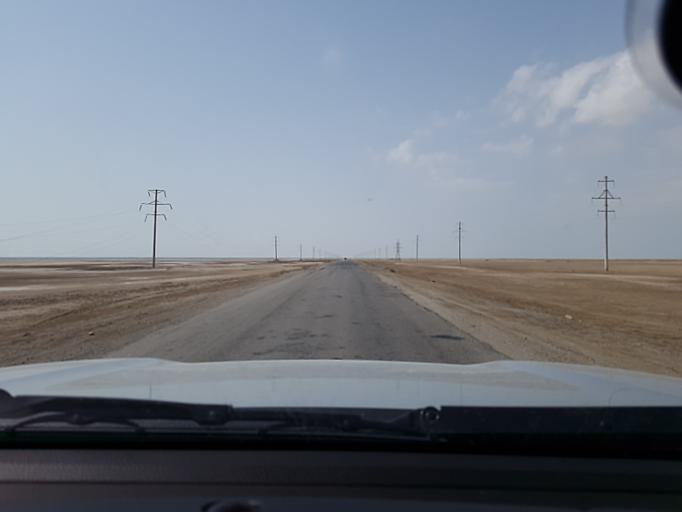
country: TM
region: Balkan
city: Gumdag
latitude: 39.0867
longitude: 54.5844
